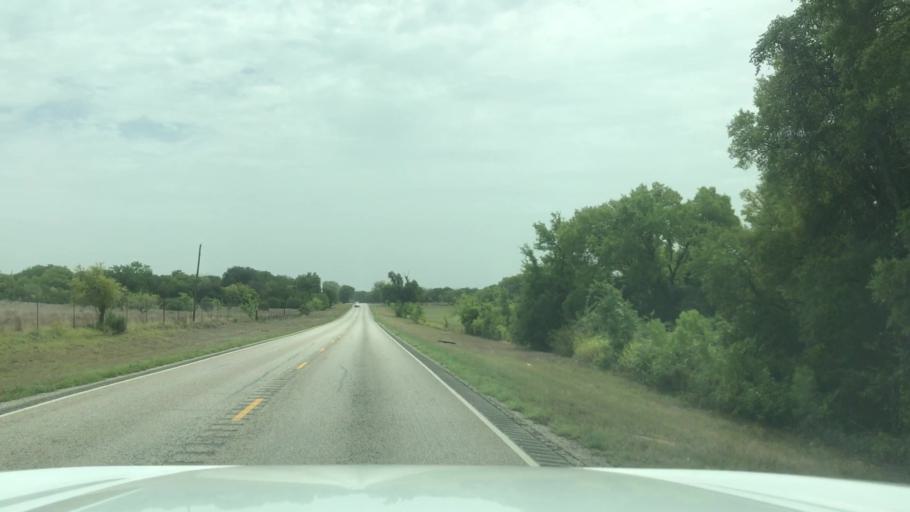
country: US
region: Texas
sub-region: Hamilton County
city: Hico
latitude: 32.0417
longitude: -98.1313
